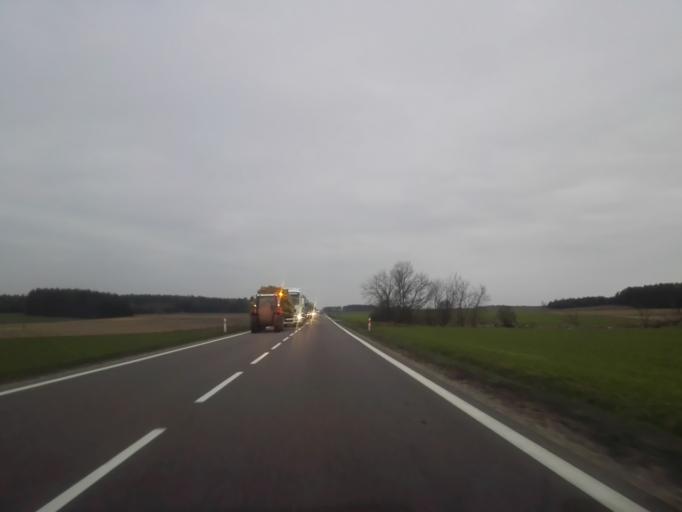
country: PL
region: Podlasie
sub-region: Powiat grajewski
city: Szczuczyn
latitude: 53.4829
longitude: 22.2164
